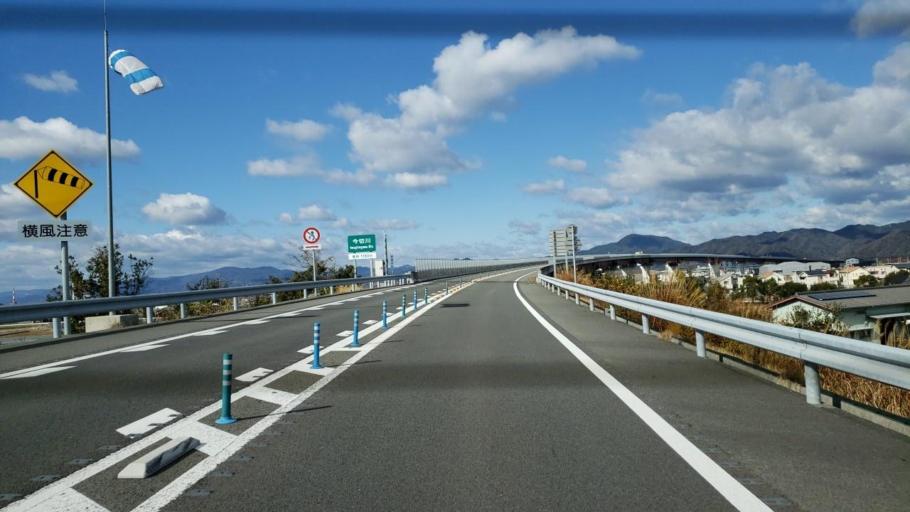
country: JP
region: Tokushima
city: Tokushima-shi
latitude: 34.1207
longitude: 134.5703
